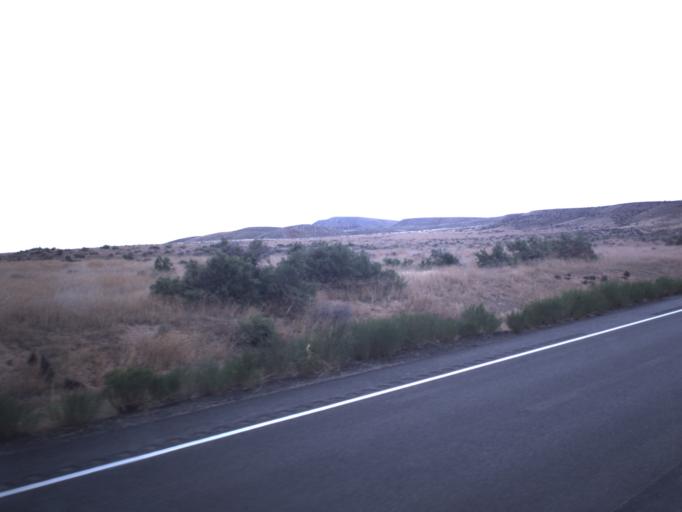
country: US
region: Utah
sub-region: Uintah County
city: Naples
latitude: 40.3082
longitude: -109.4808
